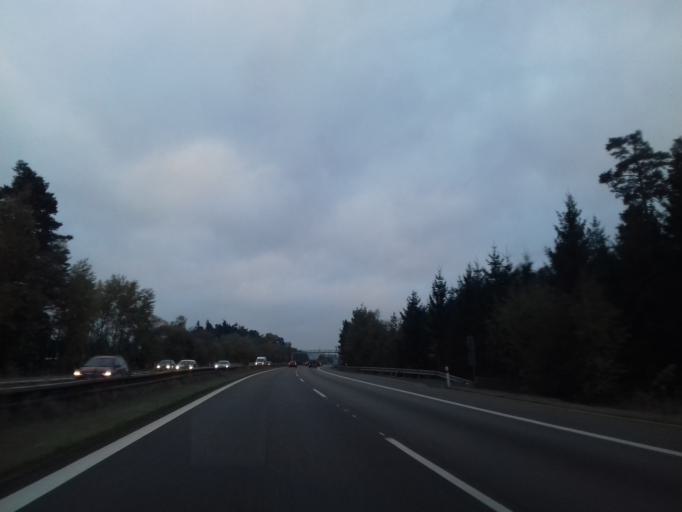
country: CZ
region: Central Bohemia
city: Zruc nad Sazavou
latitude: 49.6800
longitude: 15.1145
